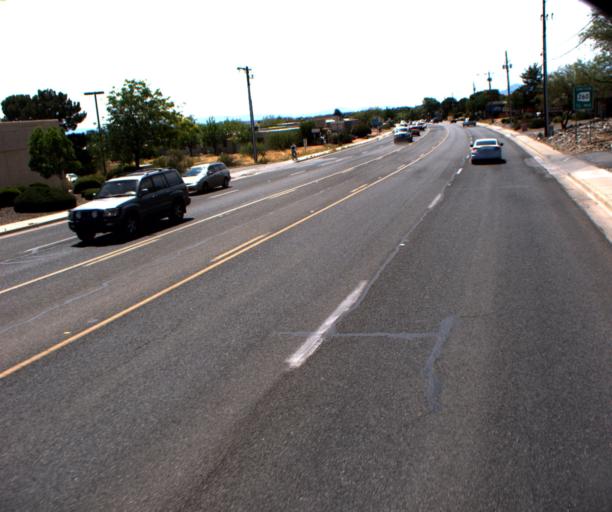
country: US
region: Arizona
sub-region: Yavapai County
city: Cottonwood
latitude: 34.7274
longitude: -112.0088
